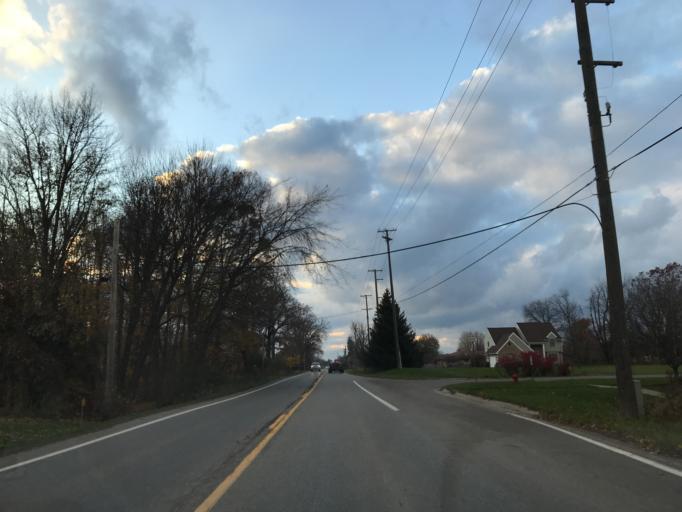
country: US
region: Michigan
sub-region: Oakland County
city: South Lyon
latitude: 42.4623
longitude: -83.6055
